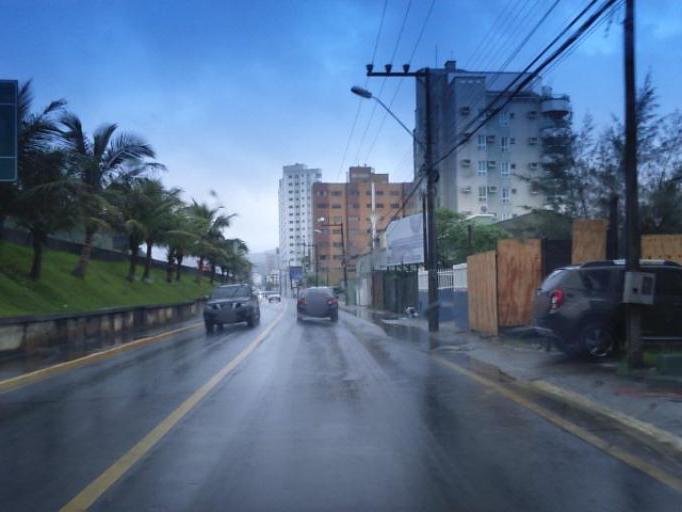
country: BR
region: Santa Catarina
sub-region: Itapema
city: Itapema
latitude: -27.1118
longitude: -48.6107
